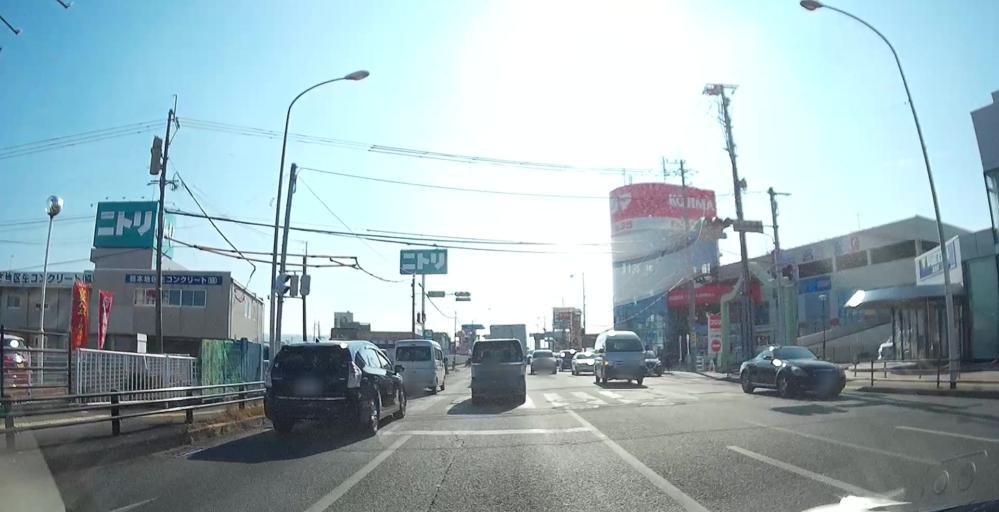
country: JP
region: Kumamoto
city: Kumamoto
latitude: 32.7610
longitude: 130.6893
